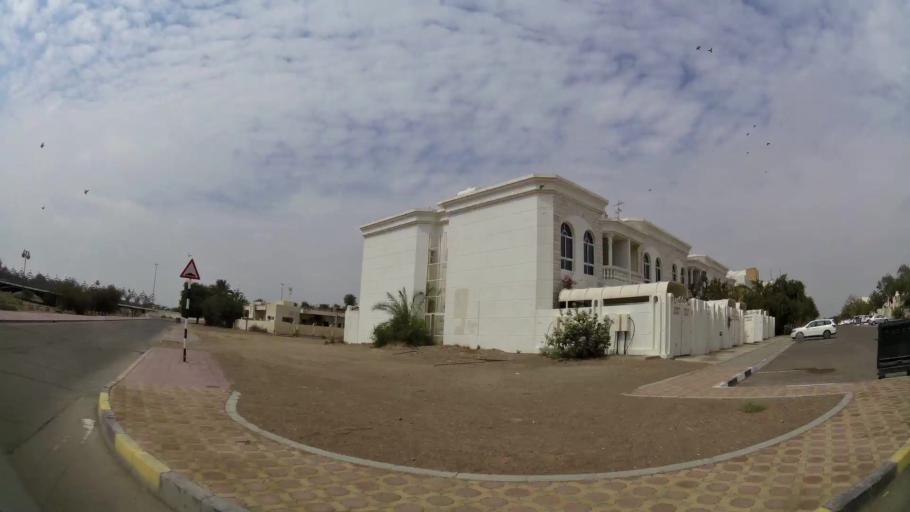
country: AE
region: Abu Dhabi
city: Al Ain
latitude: 24.2111
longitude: 55.7887
